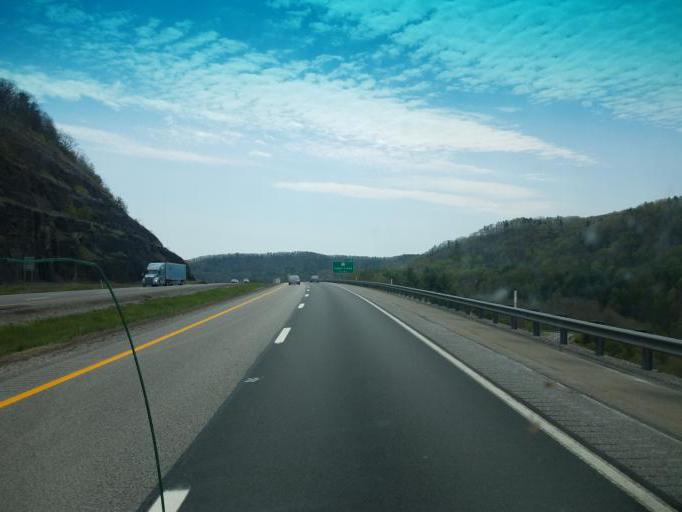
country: US
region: West Virginia
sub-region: Mercer County
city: Athens
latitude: 37.5061
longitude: -81.1169
